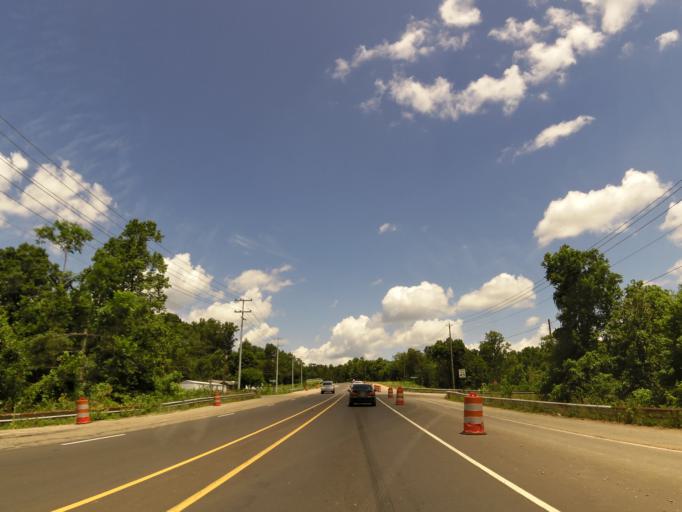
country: US
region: Tennessee
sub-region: Union County
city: Condon
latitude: 36.1328
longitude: -83.9138
